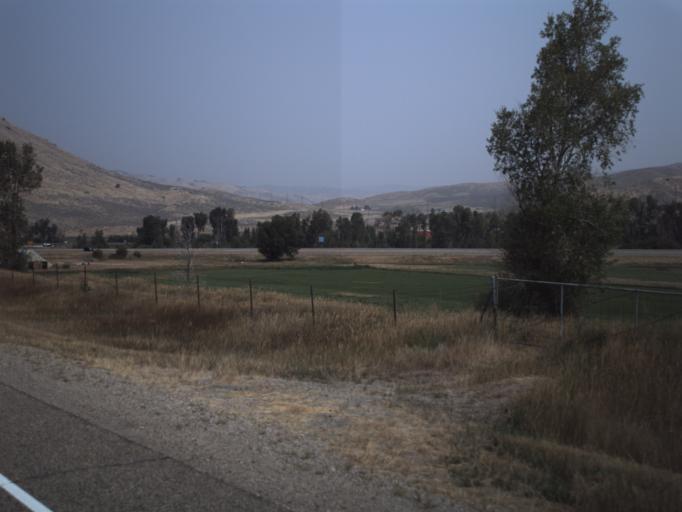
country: US
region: Utah
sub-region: Morgan County
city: Morgan
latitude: 41.0369
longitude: -111.5162
